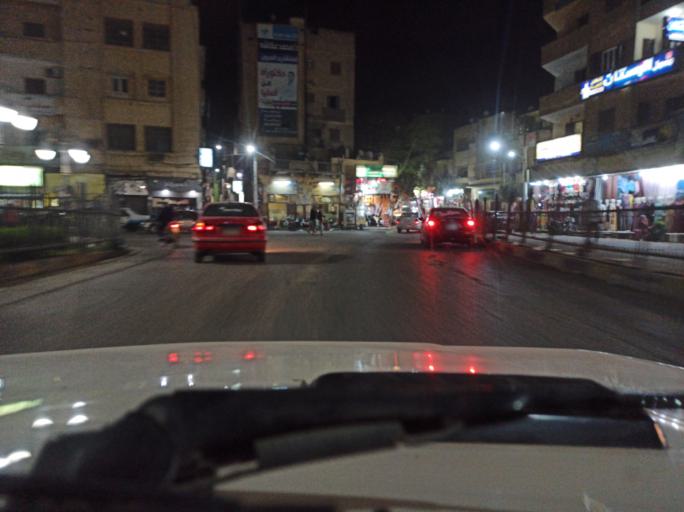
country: EG
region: Muhafazat Bani Suwayf
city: Bani Suwayf
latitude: 29.0747
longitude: 31.0939
